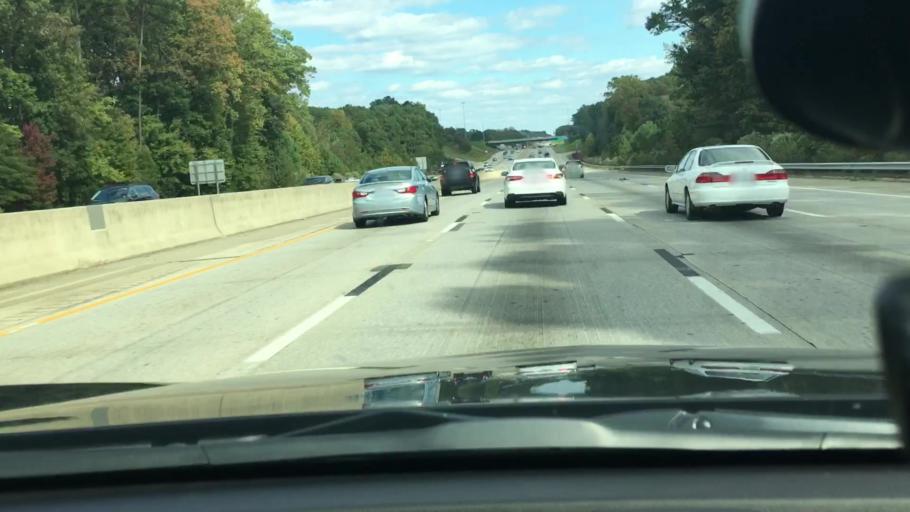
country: US
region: North Carolina
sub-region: Wake County
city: Cary
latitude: 35.7450
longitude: -78.7786
